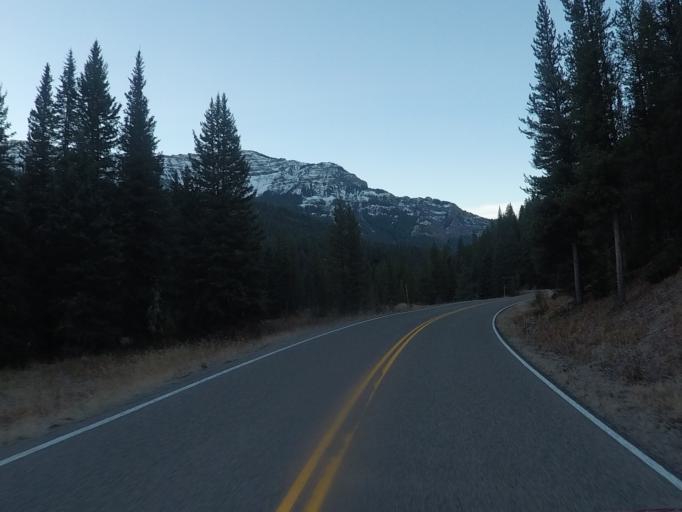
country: US
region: Montana
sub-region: Stillwater County
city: Absarokee
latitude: 44.9384
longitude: -110.0832
